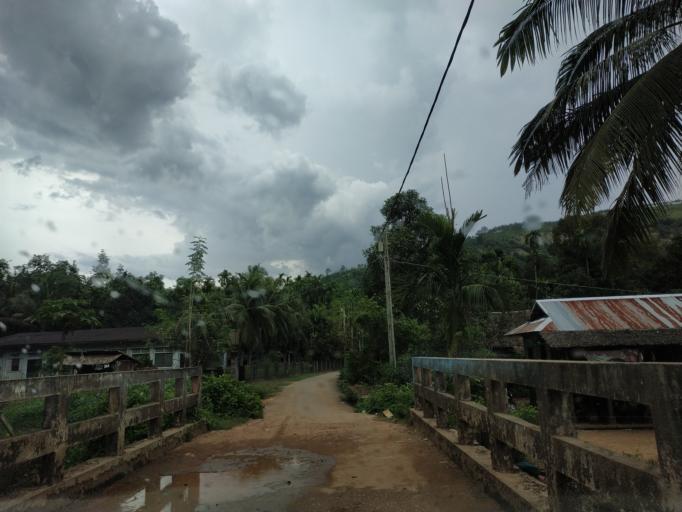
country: MM
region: Tanintharyi
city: Dawei
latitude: 13.8615
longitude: 98.2684
